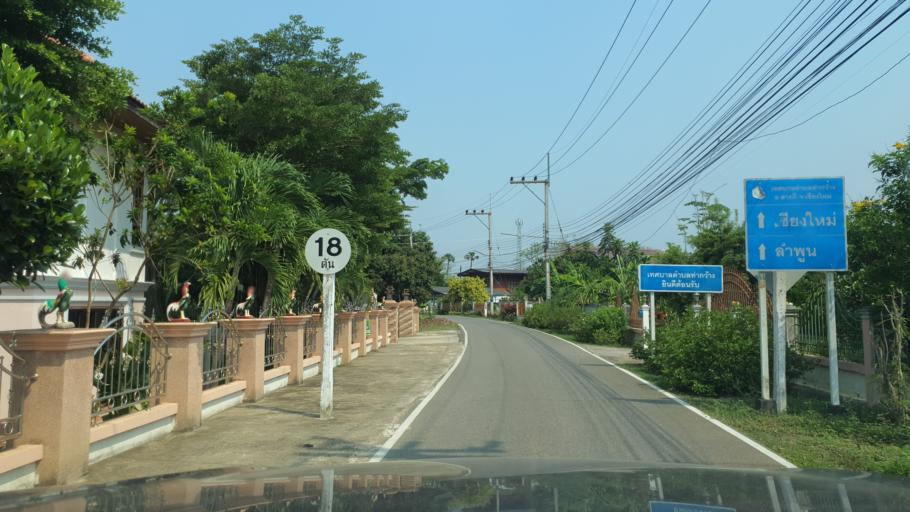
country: TH
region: Lamphun
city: Lamphun
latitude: 18.6391
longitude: 98.9927
